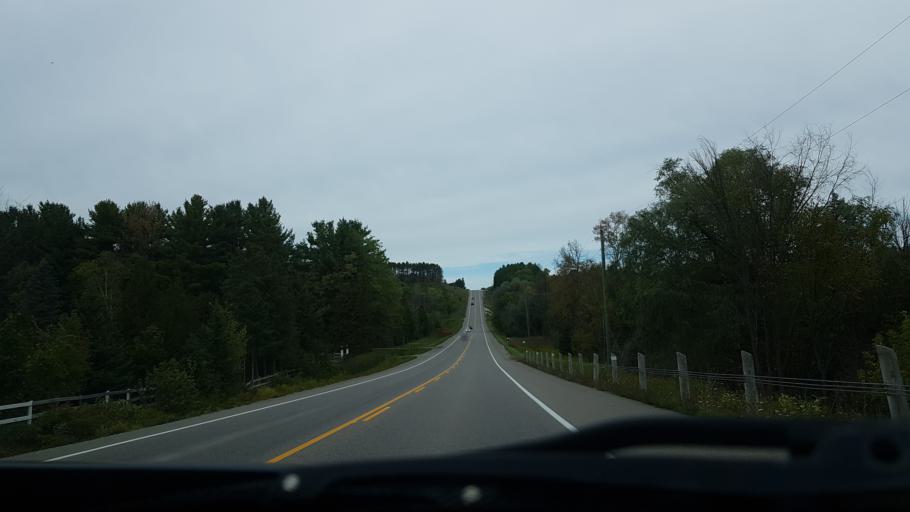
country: CA
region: Ontario
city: Orangeville
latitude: 44.0198
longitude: -80.0035
